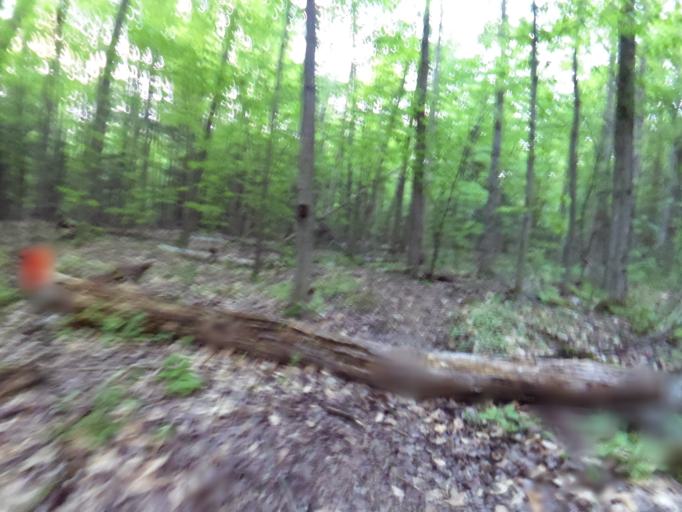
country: CA
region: Ontario
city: Bells Corners
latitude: 45.3221
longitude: -75.8151
